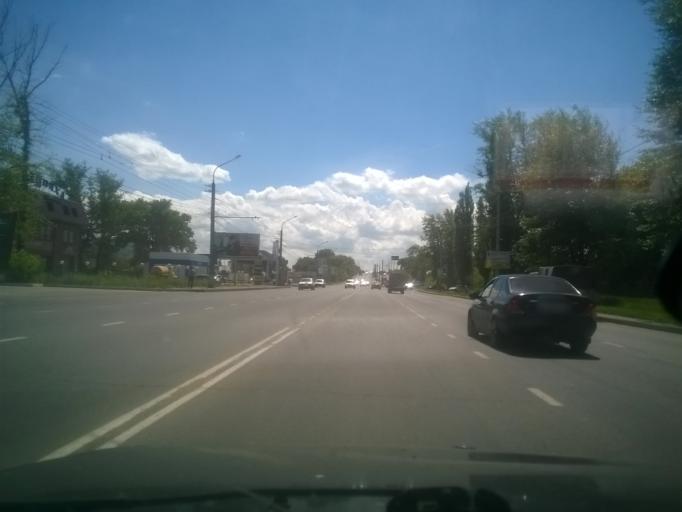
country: RU
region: Kursk
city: Kursk
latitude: 51.6597
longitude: 36.1355
